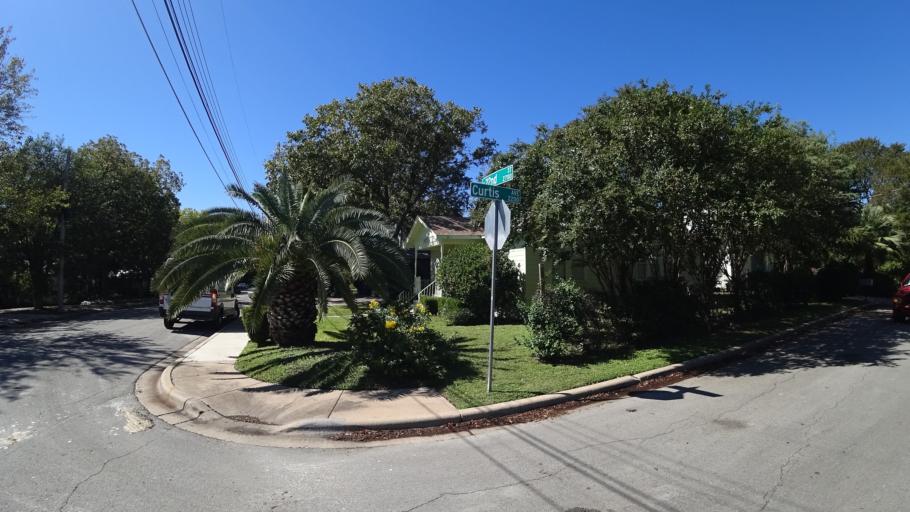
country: US
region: Texas
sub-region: Travis County
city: Austin
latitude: 30.2841
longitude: -97.7122
